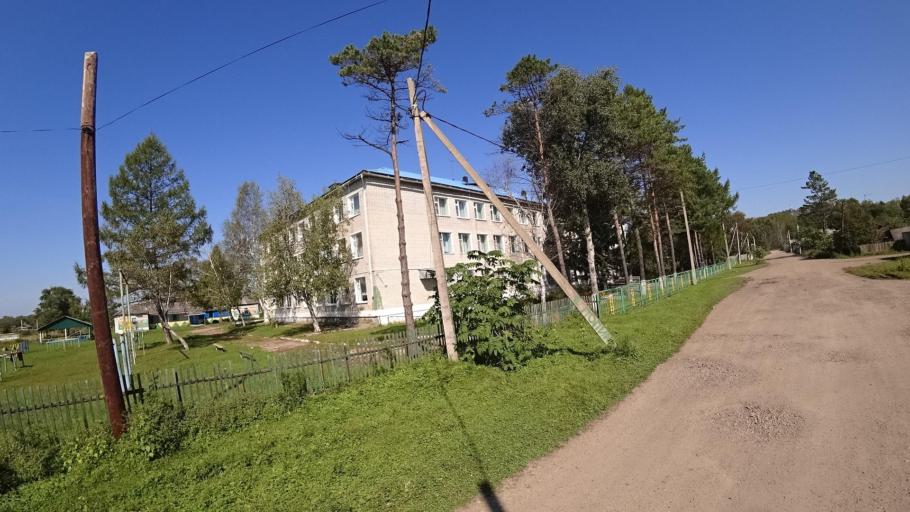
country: RU
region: Jewish Autonomous Oblast
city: Bira
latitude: 48.9969
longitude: 132.4549
